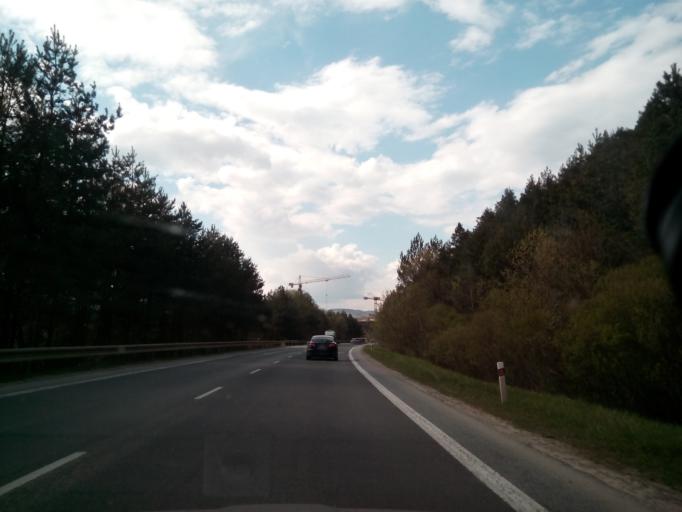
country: SK
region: Presovsky
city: Sabinov
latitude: 49.0159
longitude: 21.0423
